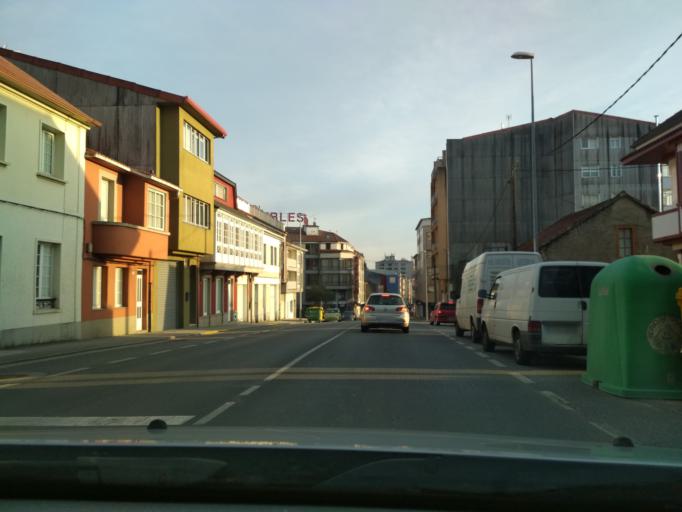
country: ES
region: Galicia
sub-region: Provincia da Coruna
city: Ordes
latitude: 43.0822
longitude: -8.4051
